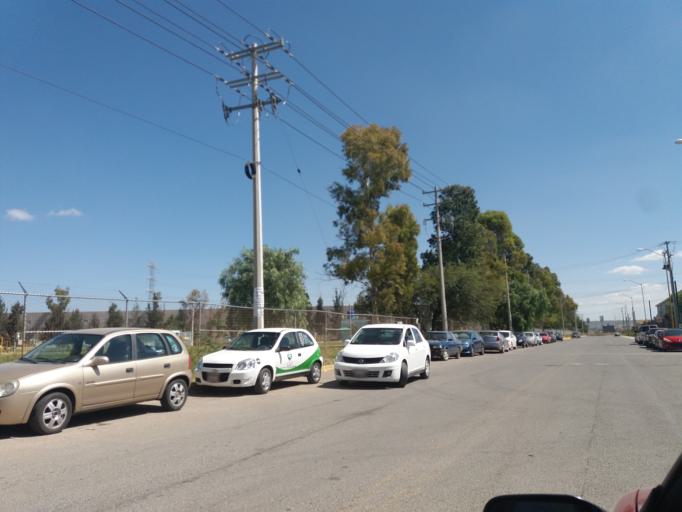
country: MX
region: Aguascalientes
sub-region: Aguascalientes
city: San Sebastian [Fraccionamiento]
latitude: 21.7990
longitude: -102.2921
